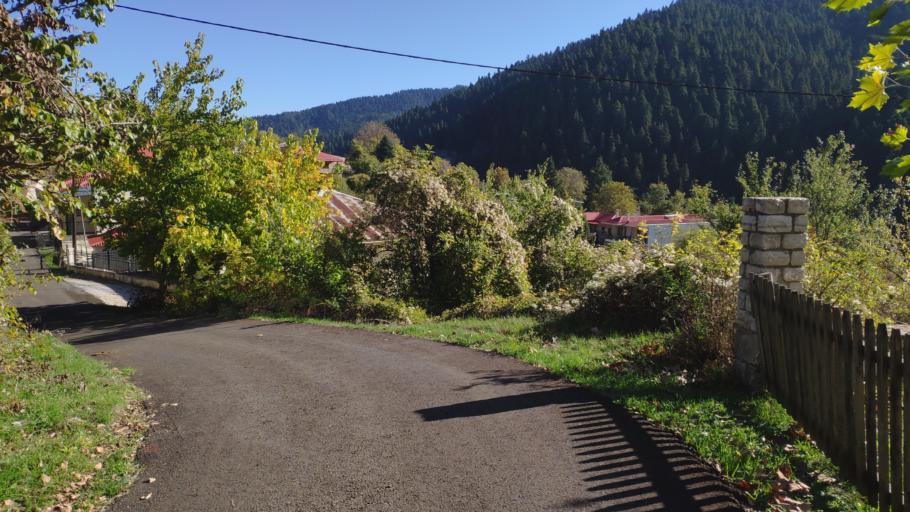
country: GR
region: Thessaly
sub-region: Trikala
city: Pyli
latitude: 39.5396
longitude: 21.4650
